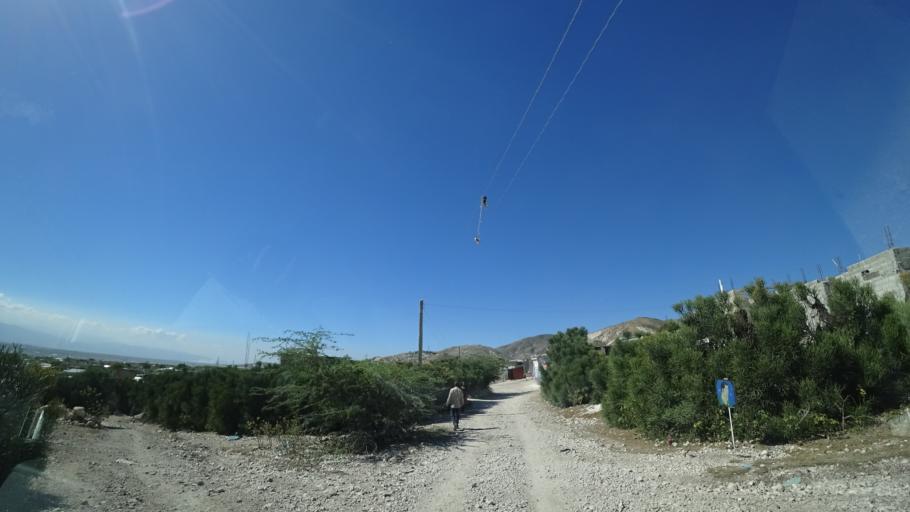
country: HT
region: Ouest
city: Croix des Bouquets
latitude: 18.6708
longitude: -72.2366
